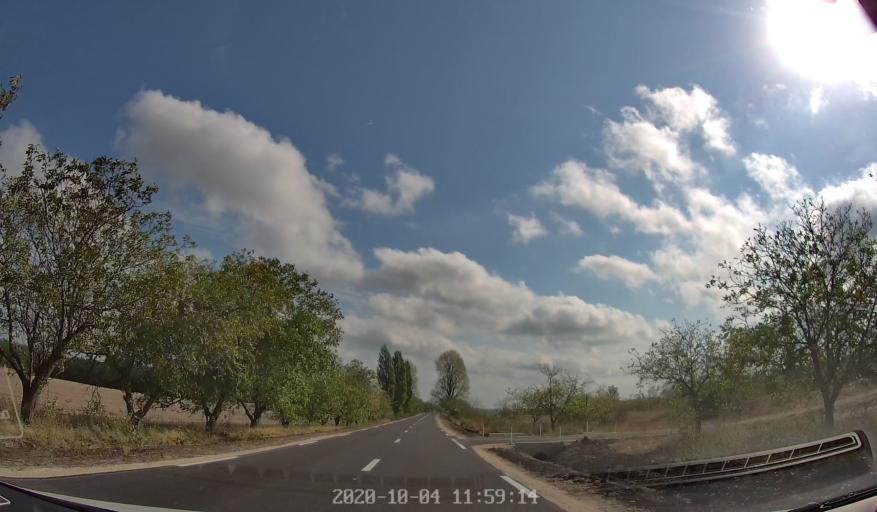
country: MD
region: Rezina
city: Saharna
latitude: 47.6326
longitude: 28.8471
